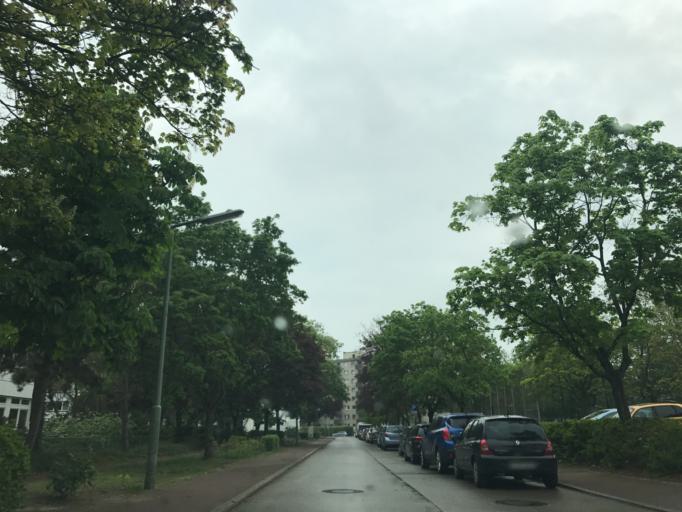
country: DE
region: Berlin
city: Staaken
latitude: 52.5479
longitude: 13.1533
